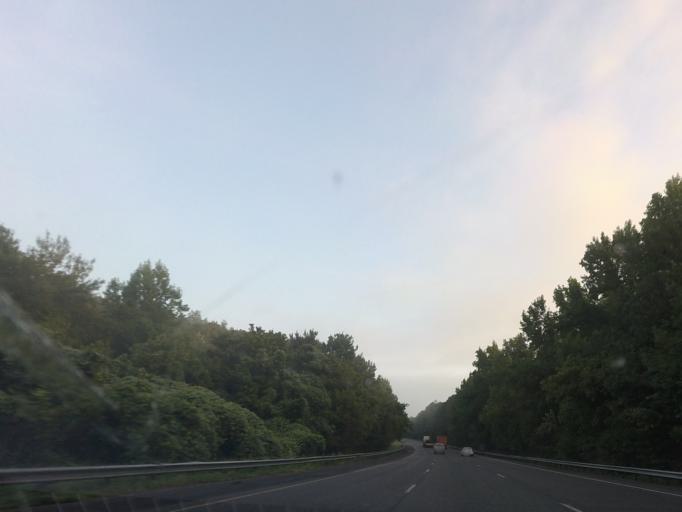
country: US
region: Georgia
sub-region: Monroe County
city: Forsyth
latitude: 33.0868
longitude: -83.9924
